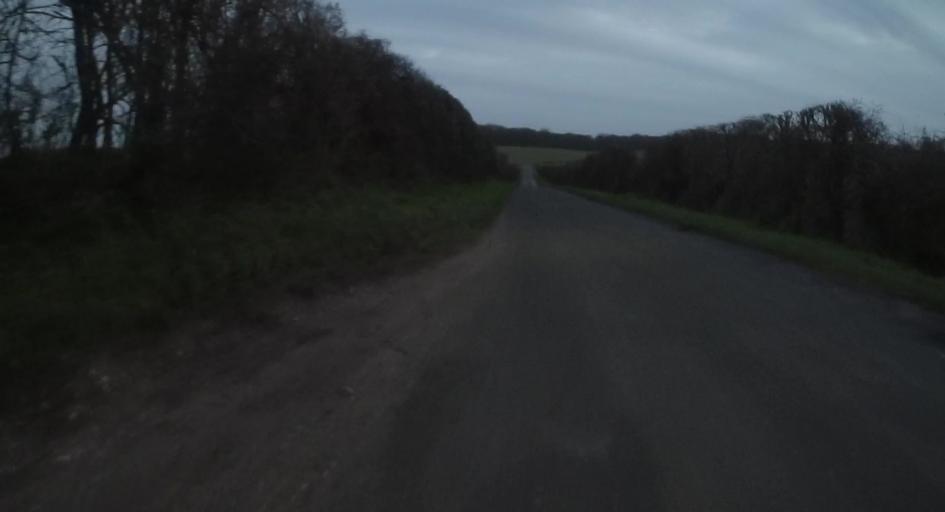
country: GB
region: England
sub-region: Hampshire
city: Overton
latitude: 51.2073
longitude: -1.2982
